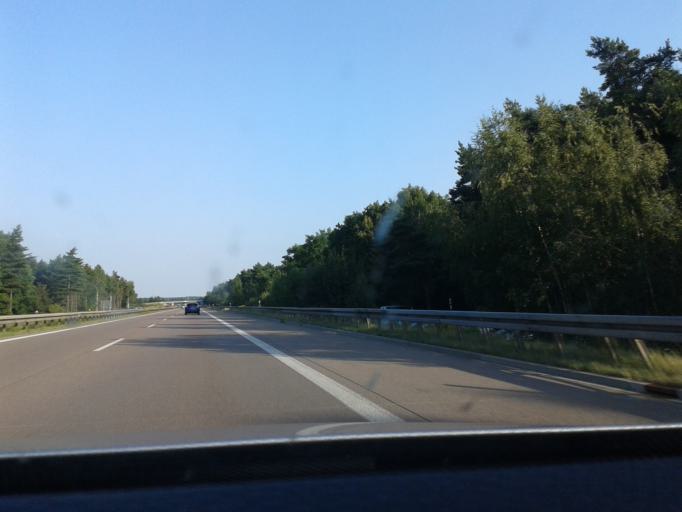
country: DE
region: Saxony
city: Naunhof
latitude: 51.2971
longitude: 12.6171
